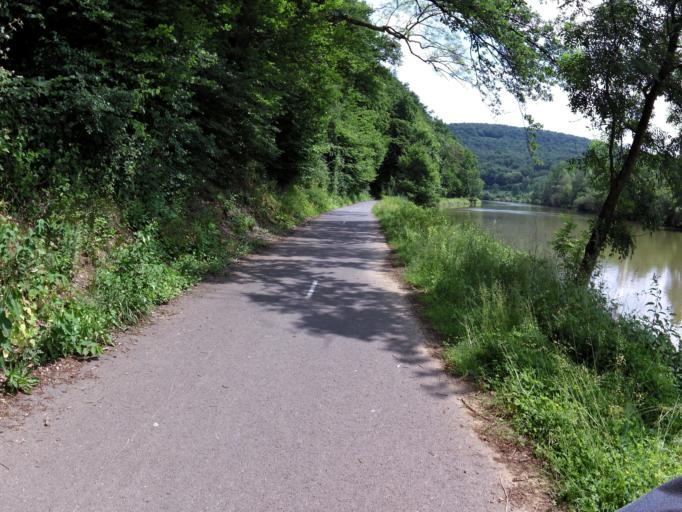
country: FR
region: Champagne-Ardenne
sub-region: Departement des Ardennes
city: Nouzonville
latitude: 49.8375
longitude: 4.7692
